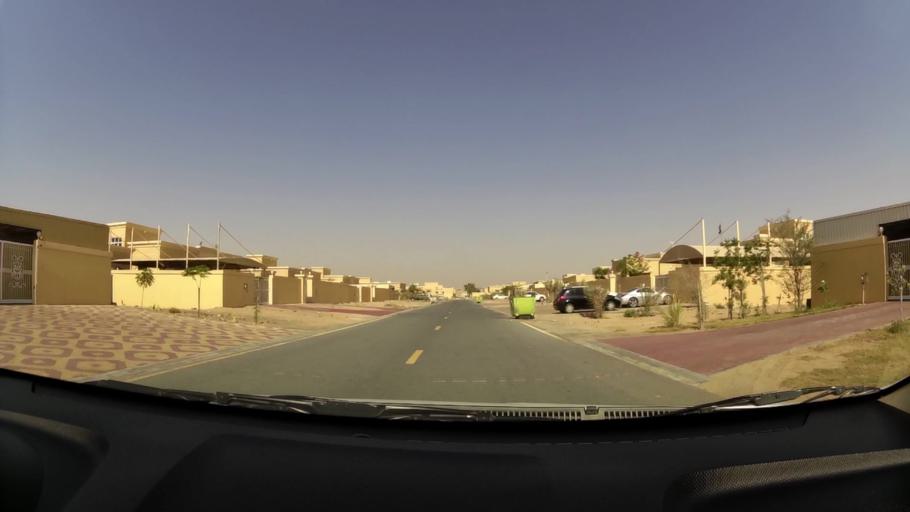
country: AE
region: Umm al Qaywayn
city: Umm al Qaywayn
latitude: 25.4772
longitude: 55.6117
